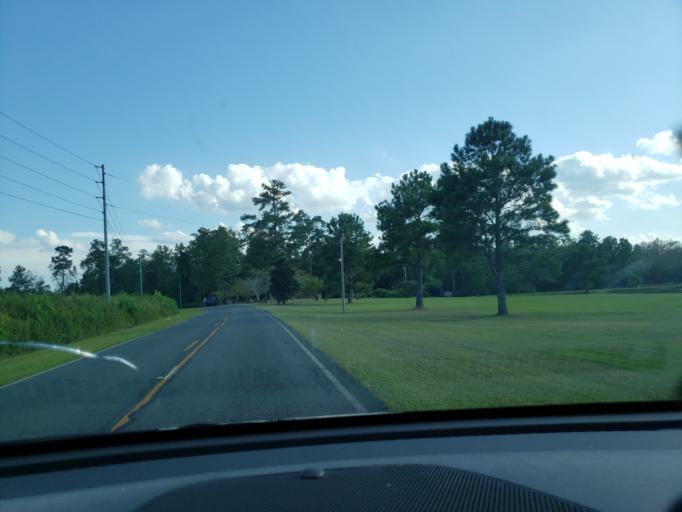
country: US
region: North Carolina
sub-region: Columbus County
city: Tabor City
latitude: 34.1635
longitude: -78.8518
